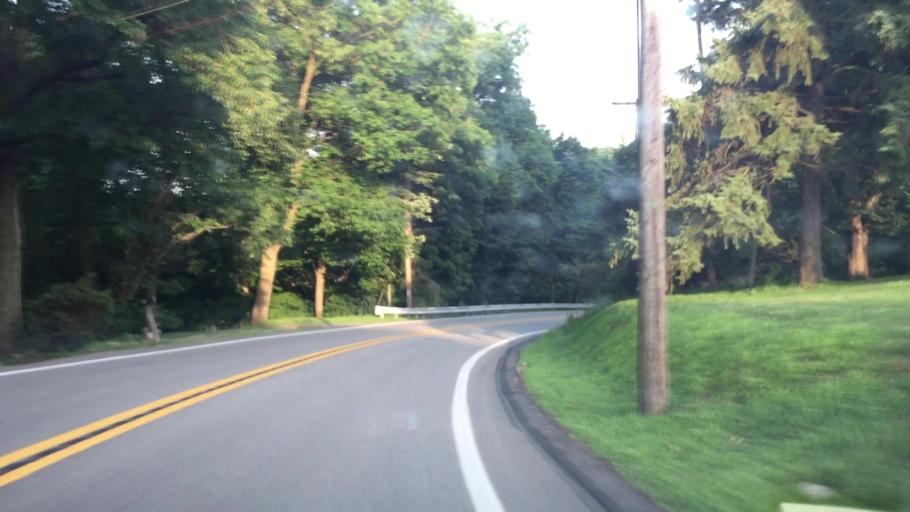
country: US
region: Pennsylvania
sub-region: Allegheny County
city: Glenshaw
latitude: 40.5356
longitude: -79.9685
